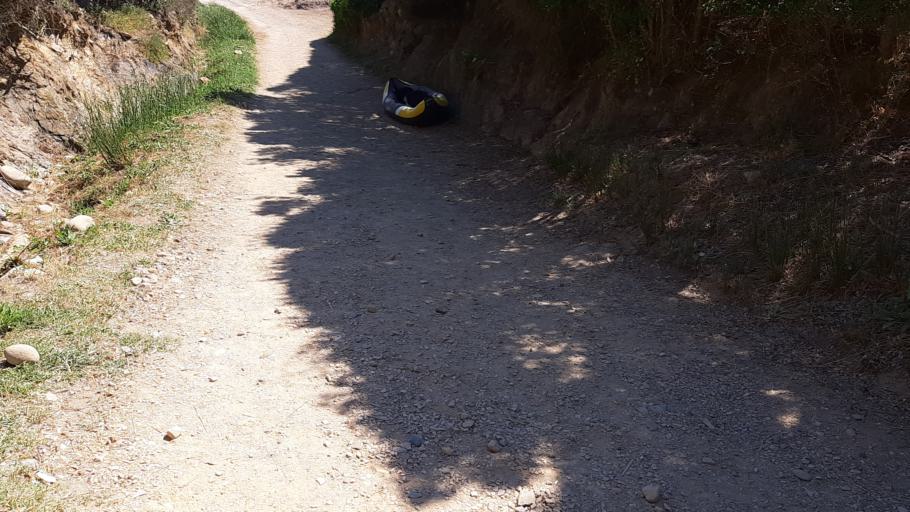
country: IT
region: Tuscany
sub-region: Provincia di Livorno
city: Portoferraio
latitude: 42.7575
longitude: 10.2960
